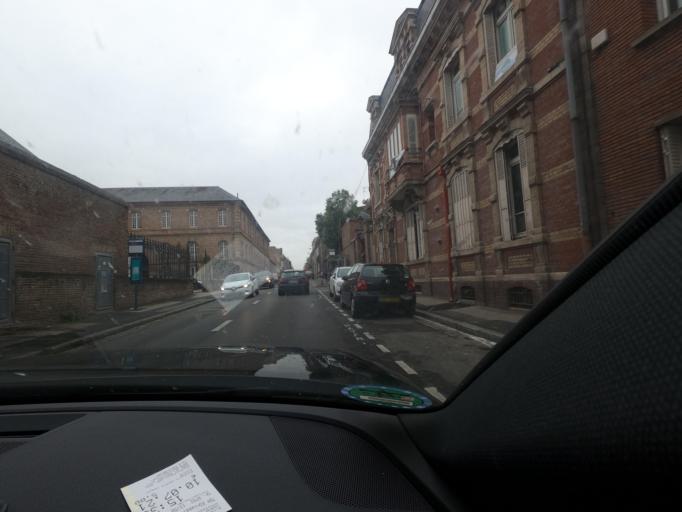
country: FR
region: Picardie
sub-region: Departement de la Somme
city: Amiens
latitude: 49.8842
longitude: 2.3041
